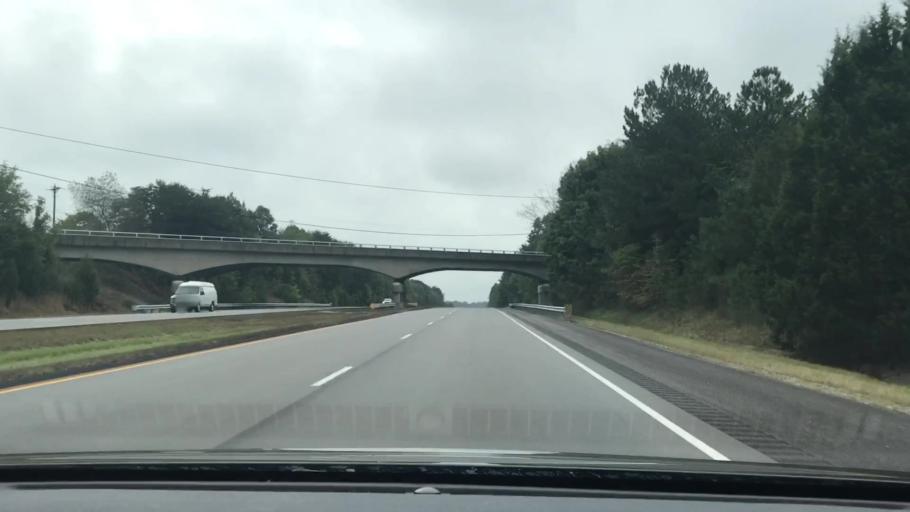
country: US
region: Kentucky
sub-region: Barren County
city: Glasgow
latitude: 36.9972
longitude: -85.8435
